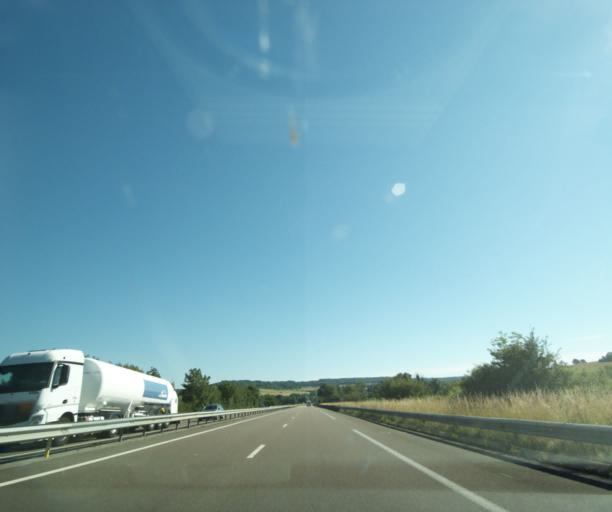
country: FR
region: Champagne-Ardenne
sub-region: Departement de la Haute-Marne
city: Rolampont
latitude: 47.9350
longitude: 5.2919
